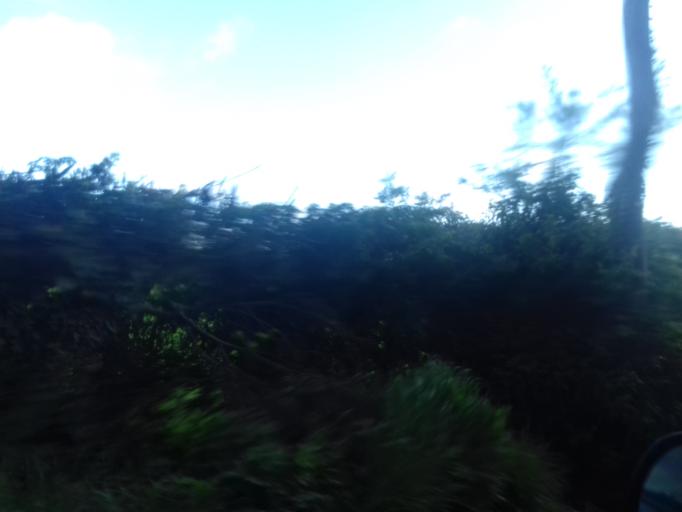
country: IE
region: Leinster
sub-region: Fingal County
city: Blanchardstown
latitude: 53.4249
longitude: -6.3469
